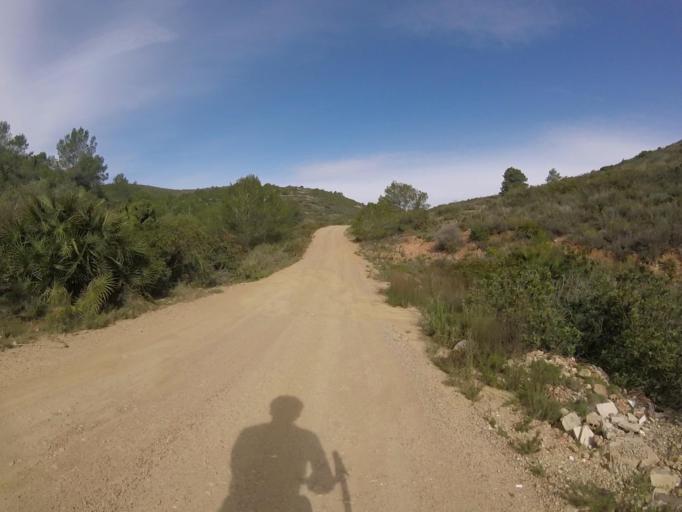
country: ES
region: Valencia
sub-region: Provincia de Castello
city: Torreblanca
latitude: 40.2012
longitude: 0.1528
